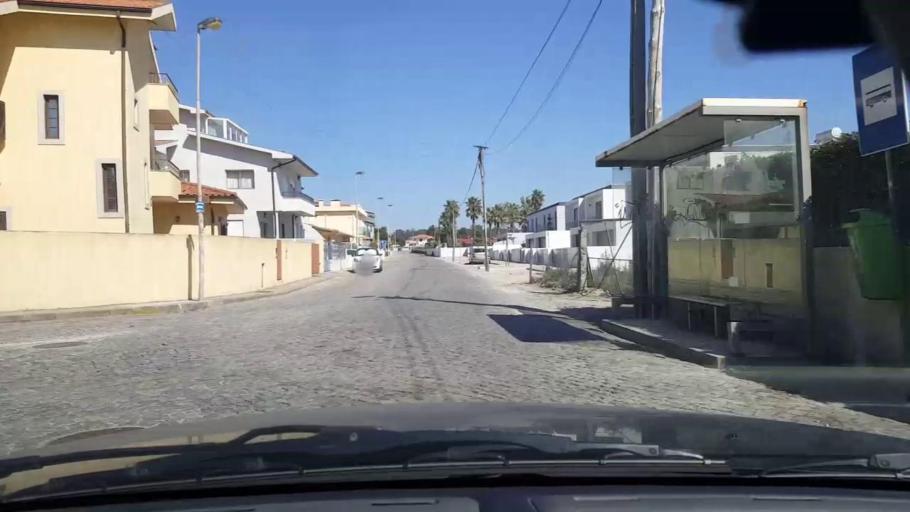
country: PT
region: Porto
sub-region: Matosinhos
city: Lavra
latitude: 41.2968
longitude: -8.7320
